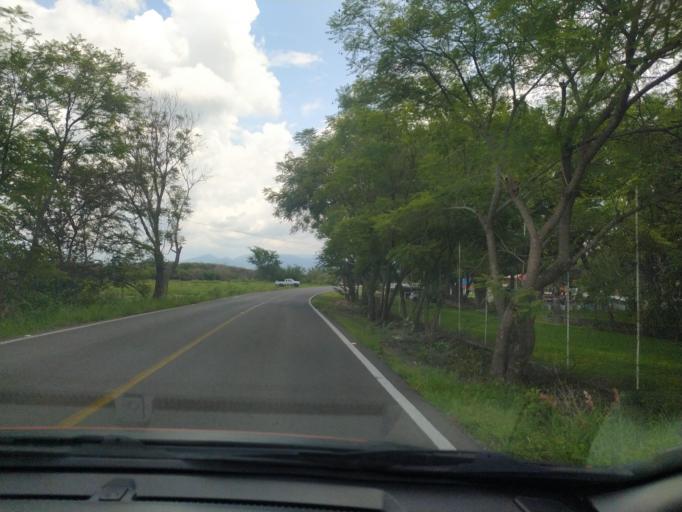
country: MX
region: Jalisco
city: Villa Corona
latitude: 20.3577
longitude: -103.6665
